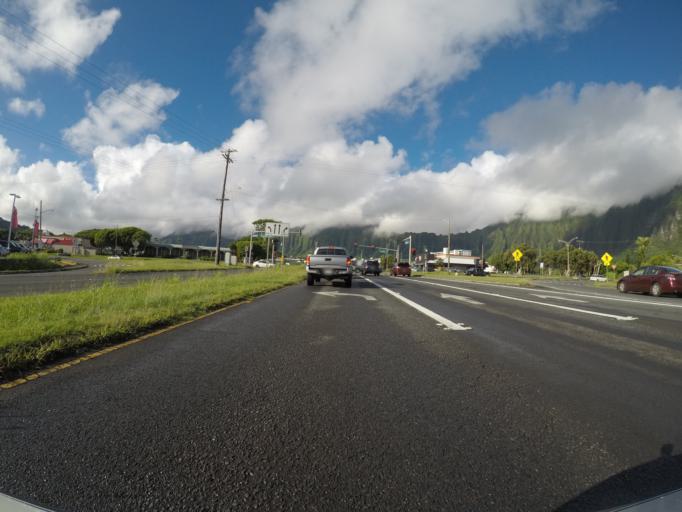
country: US
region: Hawaii
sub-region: Honolulu County
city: Kane'ohe
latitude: 21.4035
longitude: -157.7995
